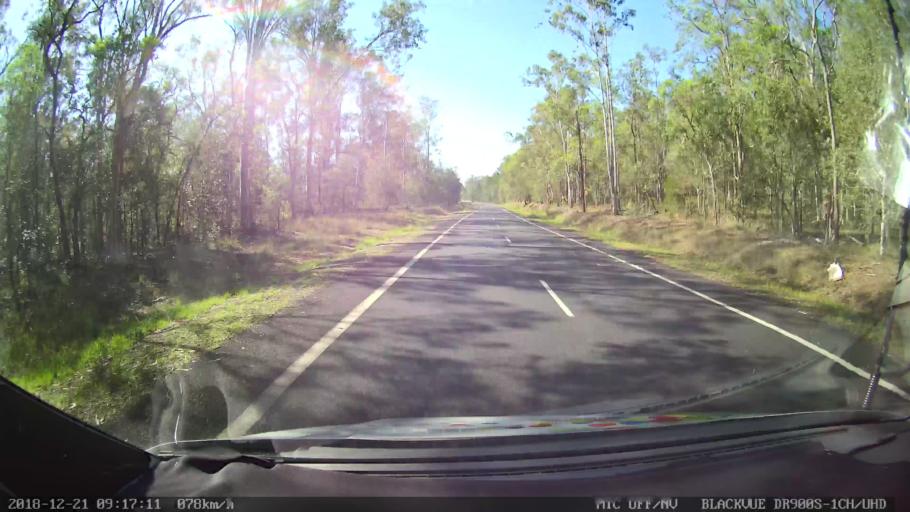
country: AU
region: New South Wales
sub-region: Clarence Valley
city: Maclean
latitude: -29.2893
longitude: 152.9896
